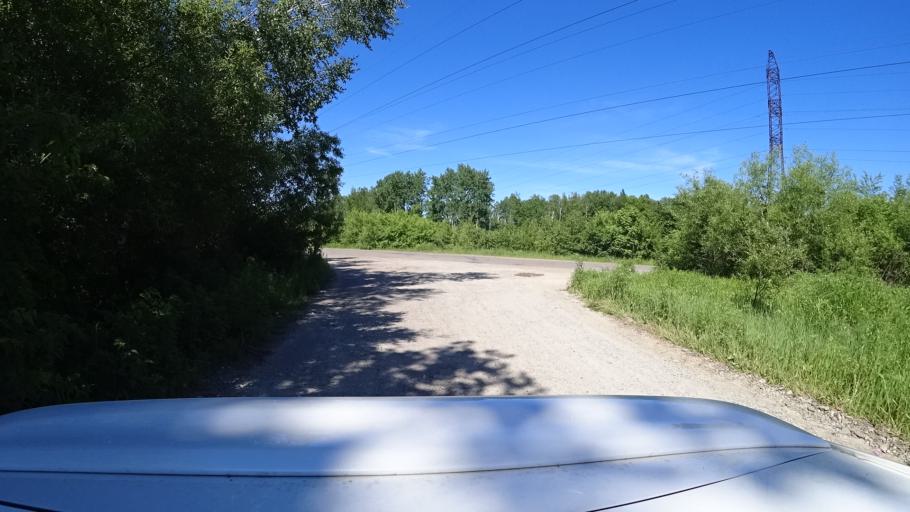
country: RU
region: Khabarovsk Krai
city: Topolevo
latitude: 48.5660
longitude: 135.1978
